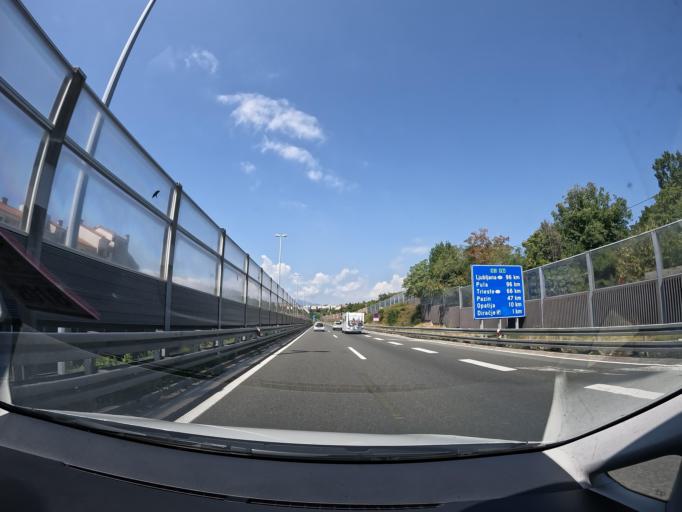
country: HR
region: Primorsko-Goranska
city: Njivice
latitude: 45.1259
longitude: 14.3809
